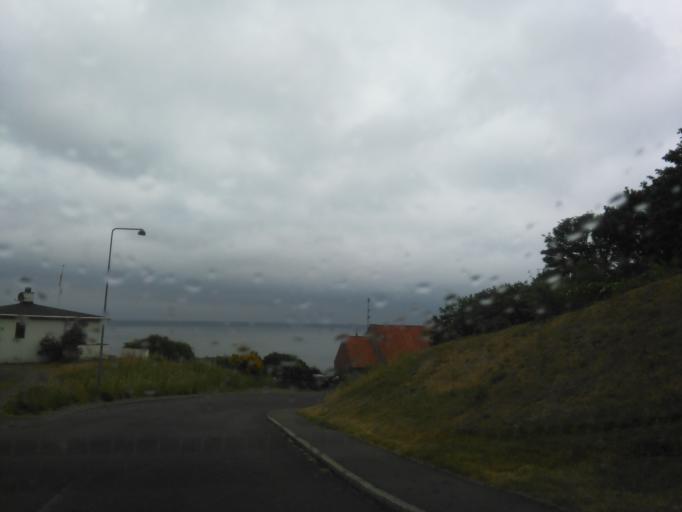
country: DK
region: Capital Region
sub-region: Bornholm Kommune
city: Ronne
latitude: 55.2472
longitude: 14.7380
